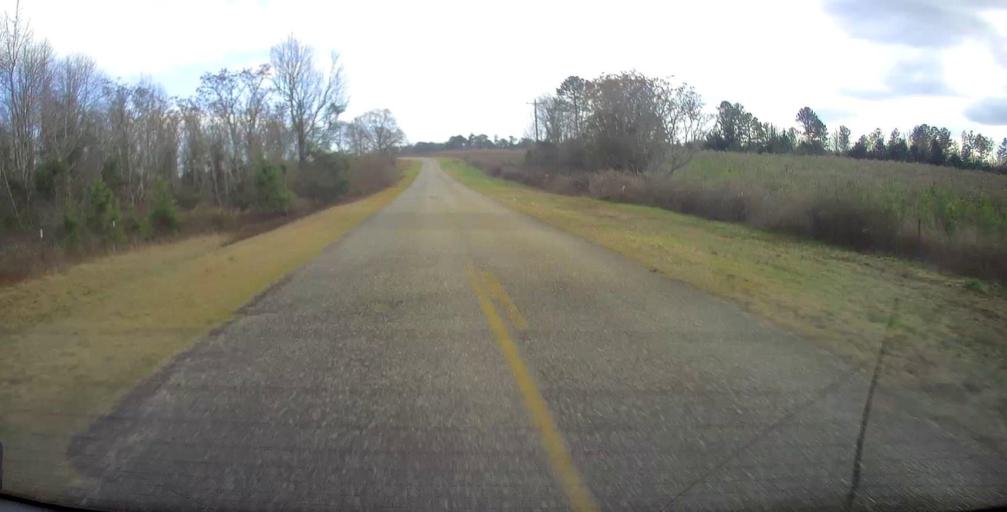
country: US
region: Georgia
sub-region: Marion County
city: Buena Vista
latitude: 32.4161
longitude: -84.4118
